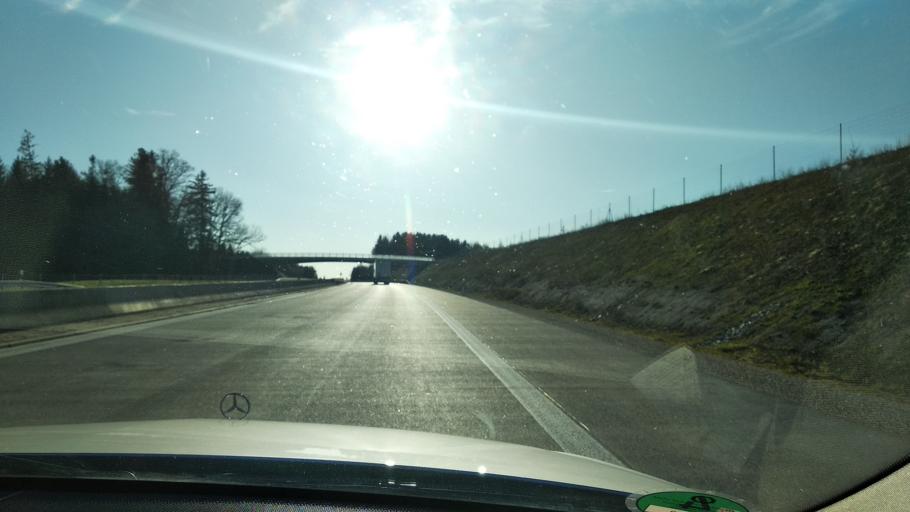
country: DE
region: Bavaria
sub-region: Upper Bavaria
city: Buch am Buchrain
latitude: 48.2425
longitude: 12.0165
